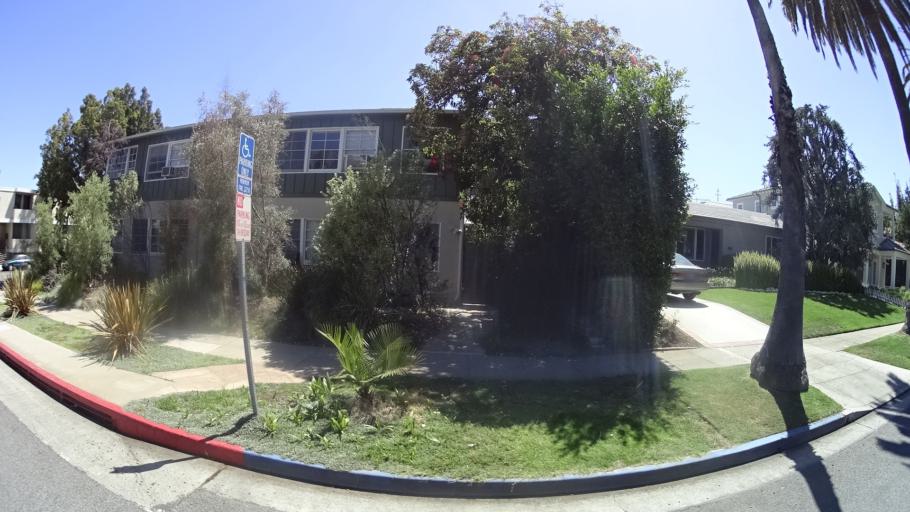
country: US
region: California
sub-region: Los Angeles County
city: Santa Monica
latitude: 34.0355
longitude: -118.4918
